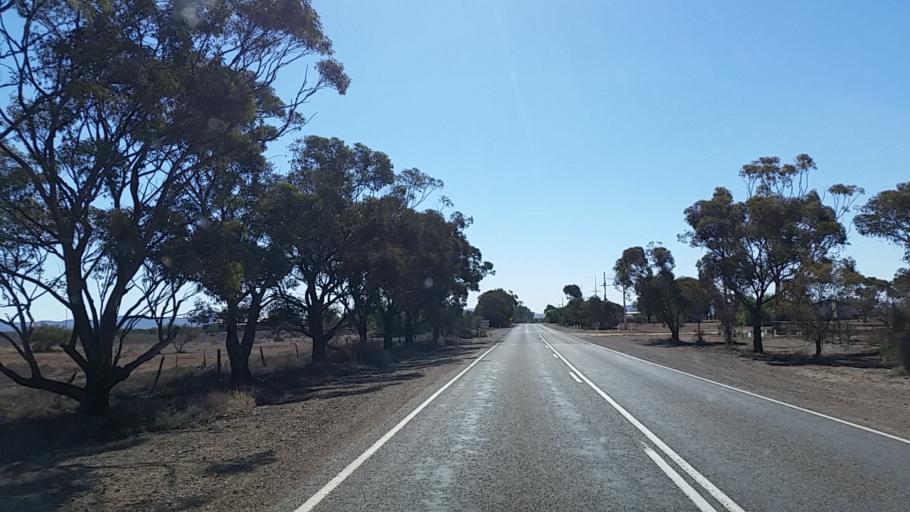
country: AU
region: South Australia
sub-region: Flinders Ranges
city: Quorn
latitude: -32.0722
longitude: 138.4954
